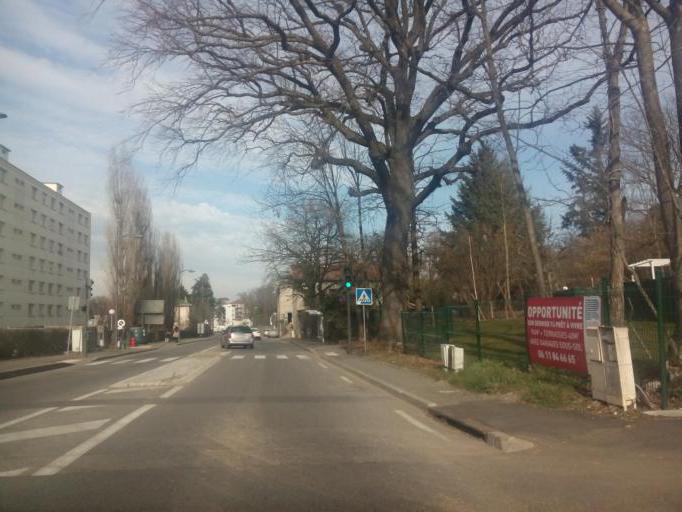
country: FR
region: Rhone-Alpes
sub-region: Departement du Rhone
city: Francheville
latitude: 45.7475
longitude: 4.7724
